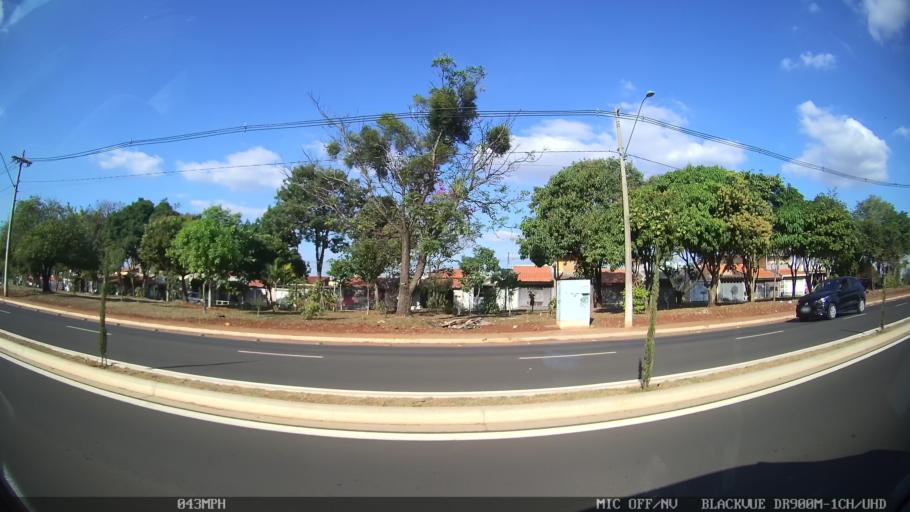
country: BR
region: Sao Paulo
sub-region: Nova Odessa
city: Nova Odessa
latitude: -22.8005
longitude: -47.3169
